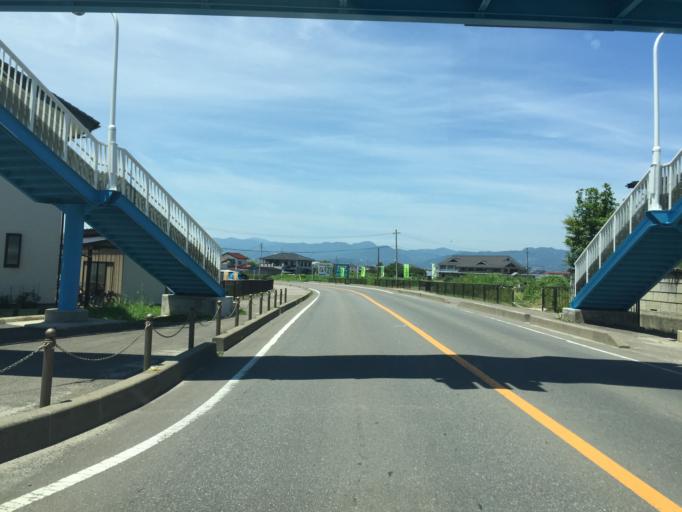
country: JP
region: Fukushima
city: Fukushima-shi
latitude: 37.7713
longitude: 140.5091
